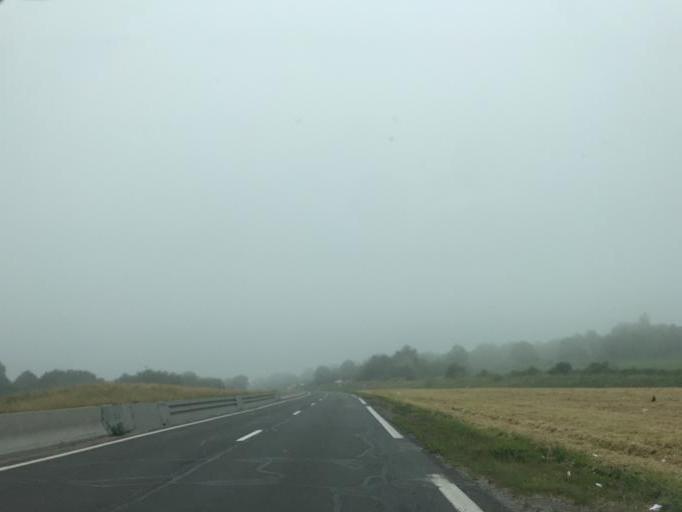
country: FR
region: Ile-de-France
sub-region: Departement de Seine-et-Marne
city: Saint-Thibault-des-Vignes
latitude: 48.8663
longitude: 2.6796
